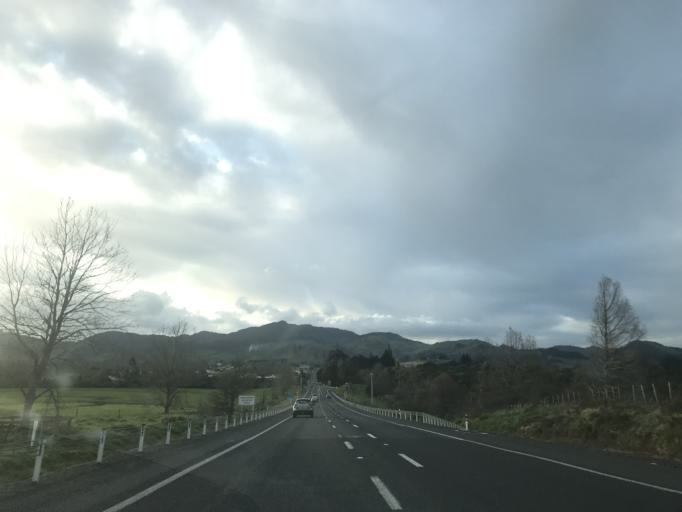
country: NZ
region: Waikato
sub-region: Hauraki District
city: Waihi
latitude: -37.3995
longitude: 175.8530
